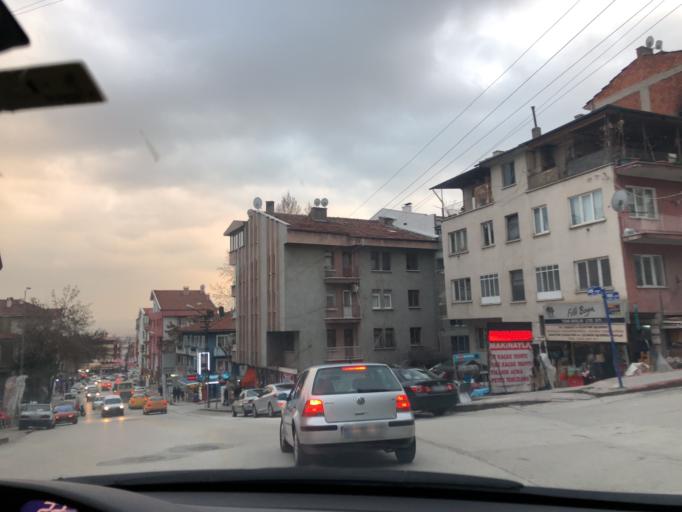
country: TR
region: Ankara
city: Ankara
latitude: 39.9686
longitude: 32.8079
